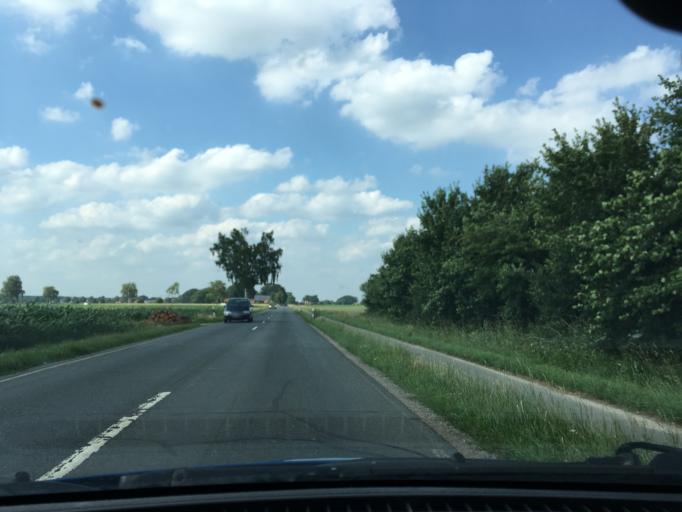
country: DE
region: Lower Saxony
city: Bendestorf
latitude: 53.3538
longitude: 9.9410
